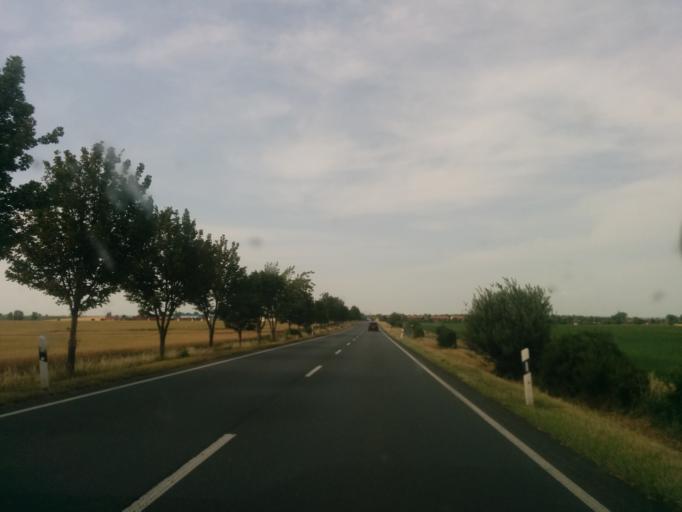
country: DE
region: Thuringia
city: Gebesee
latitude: 51.1010
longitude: 10.9295
